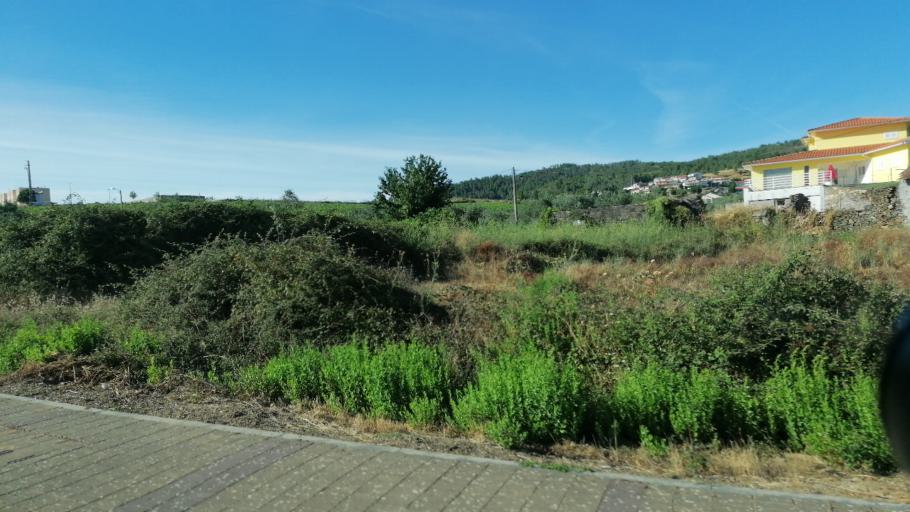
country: PT
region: Vila Real
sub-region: Murca
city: Murca
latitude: 41.4100
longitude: -7.4550
